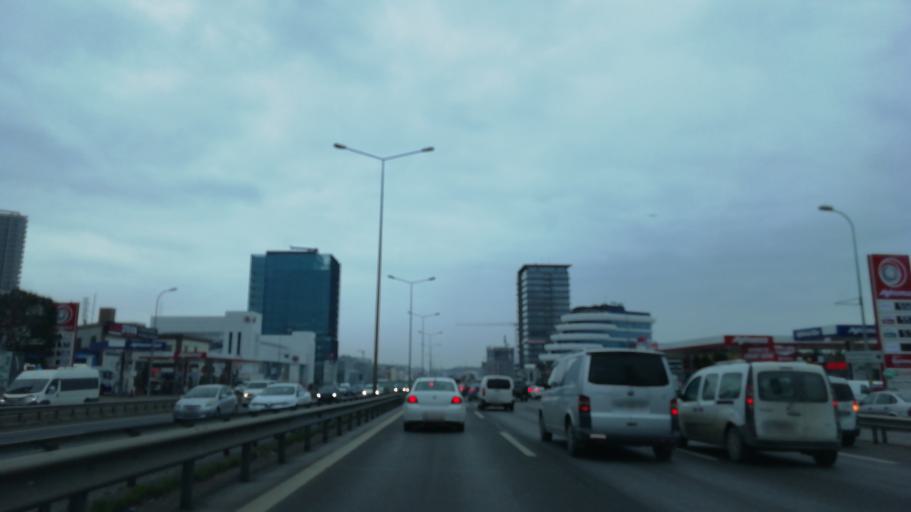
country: TR
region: Istanbul
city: Pendik
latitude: 40.8974
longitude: 29.2245
